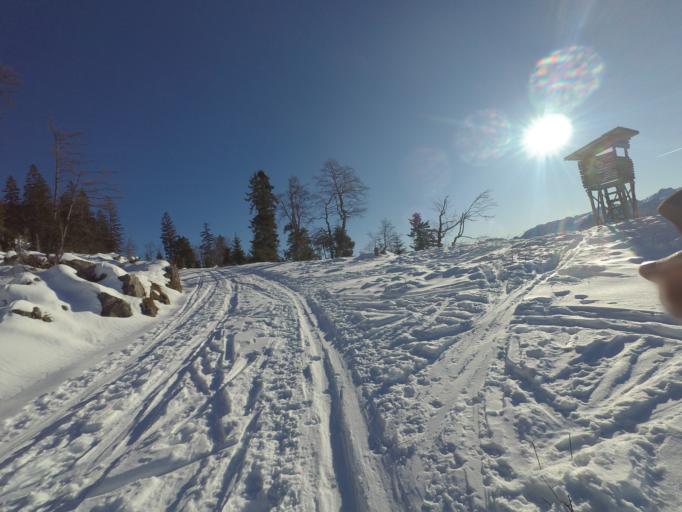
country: AT
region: Salzburg
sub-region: Politischer Bezirk Hallein
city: Scheffau am Tennengebirge
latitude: 47.6331
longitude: 13.2527
